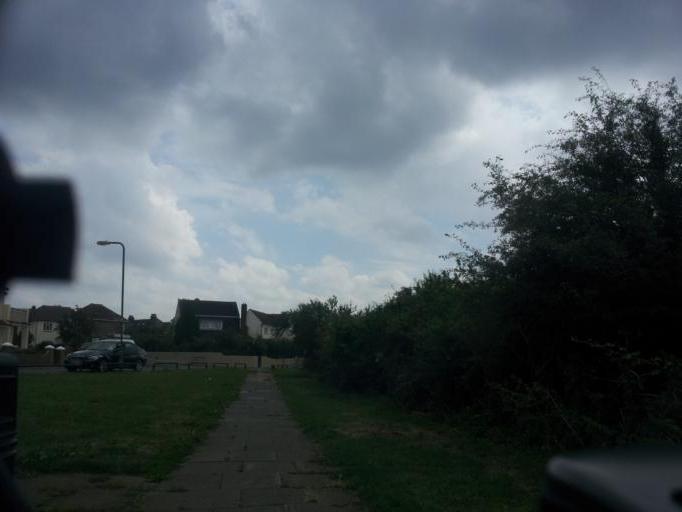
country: GB
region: England
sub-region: Kent
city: Gillingham
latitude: 51.3683
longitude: 0.5570
